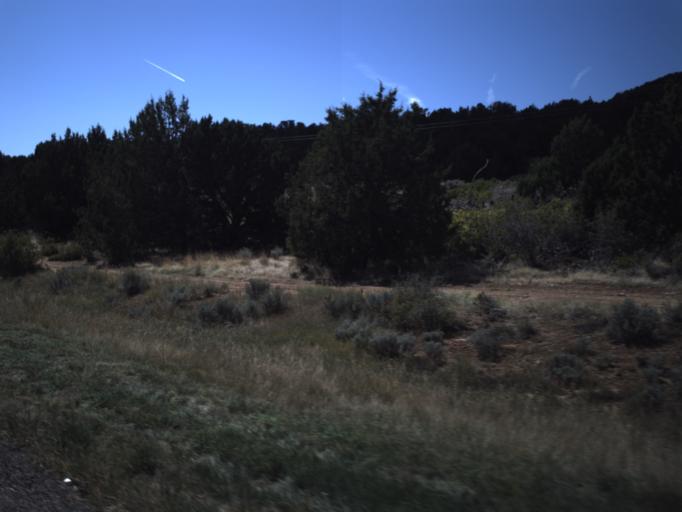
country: US
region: Utah
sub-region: Washington County
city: Enterprise
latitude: 37.5138
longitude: -113.6342
